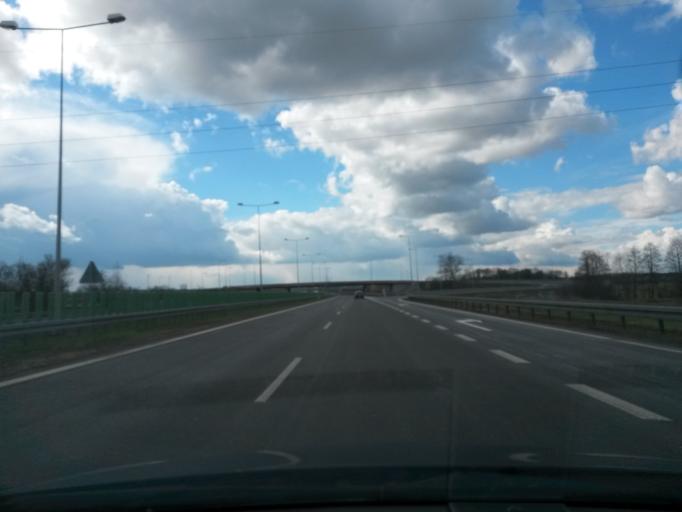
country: PL
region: Greater Poland Voivodeship
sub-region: Powiat turecki
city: Brudzew
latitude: 52.1401
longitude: 18.6118
